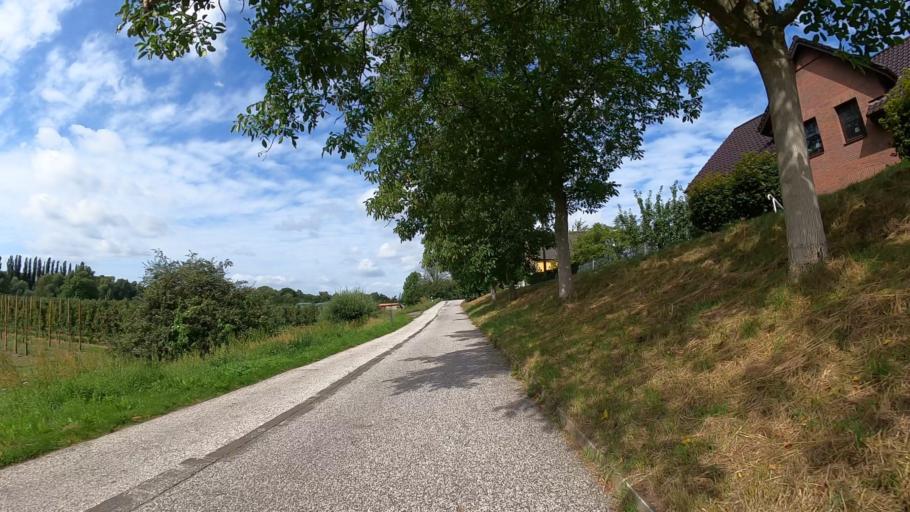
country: DE
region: Hamburg
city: Altona
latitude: 53.5203
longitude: 9.8832
